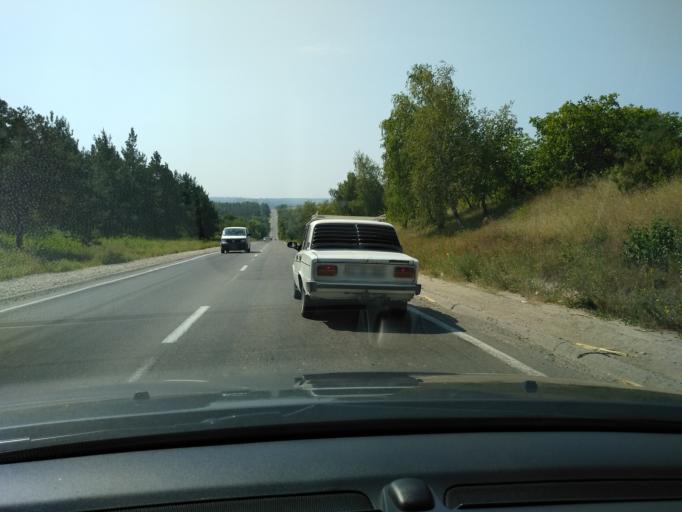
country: MD
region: Chisinau
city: Stauceni
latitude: 47.0745
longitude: 28.8131
